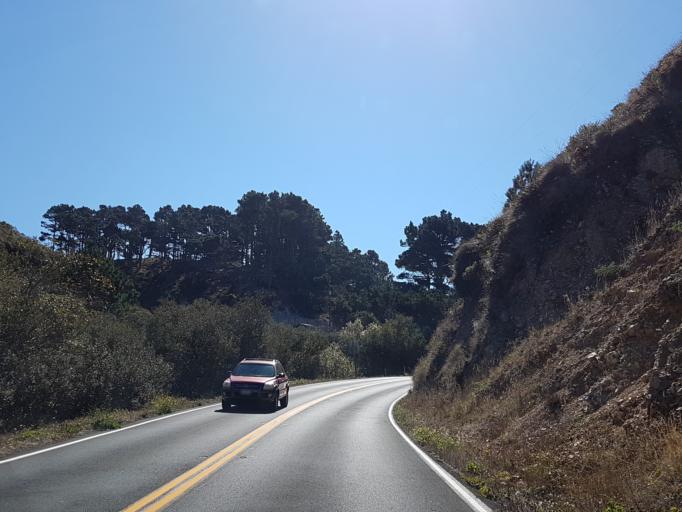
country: US
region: California
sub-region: Sonoma County
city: Sea Ranch
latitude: 38.9040
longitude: -123.6916
